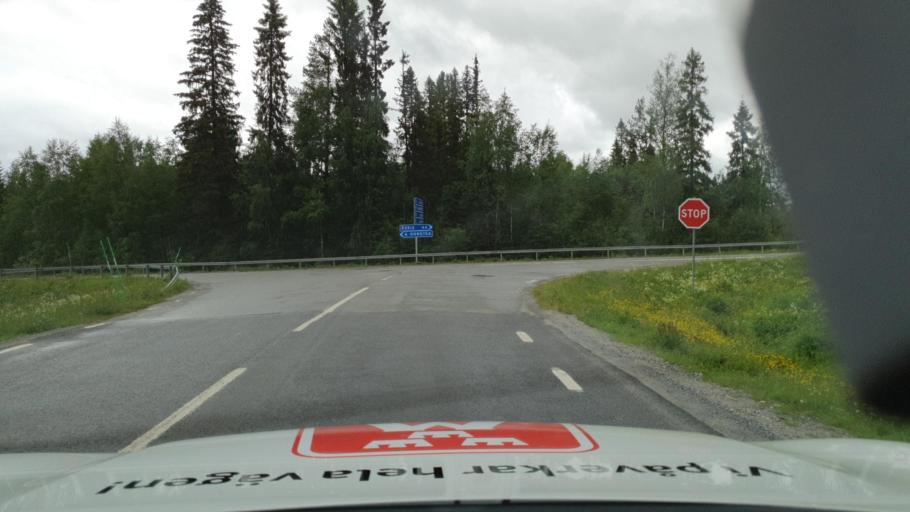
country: SE
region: Vaesterbotten
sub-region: Dorotea Kommun
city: Dorotea
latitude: 64.2487
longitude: 16.5293
